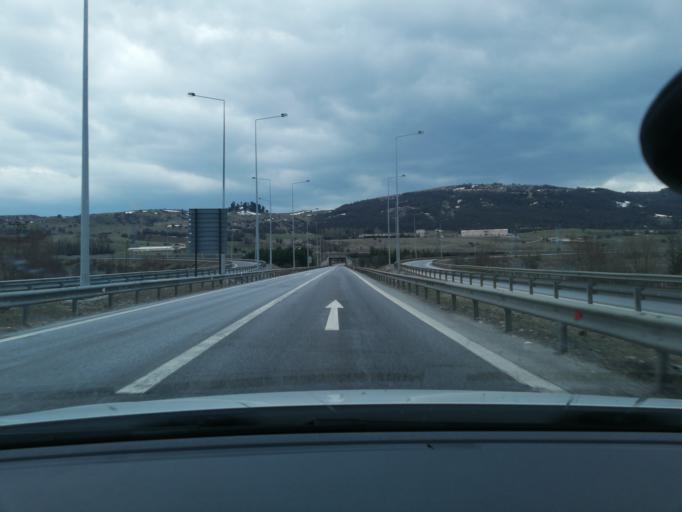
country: TR
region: Bolu
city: Yenicaga
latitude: 40.7668
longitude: 32.0091
